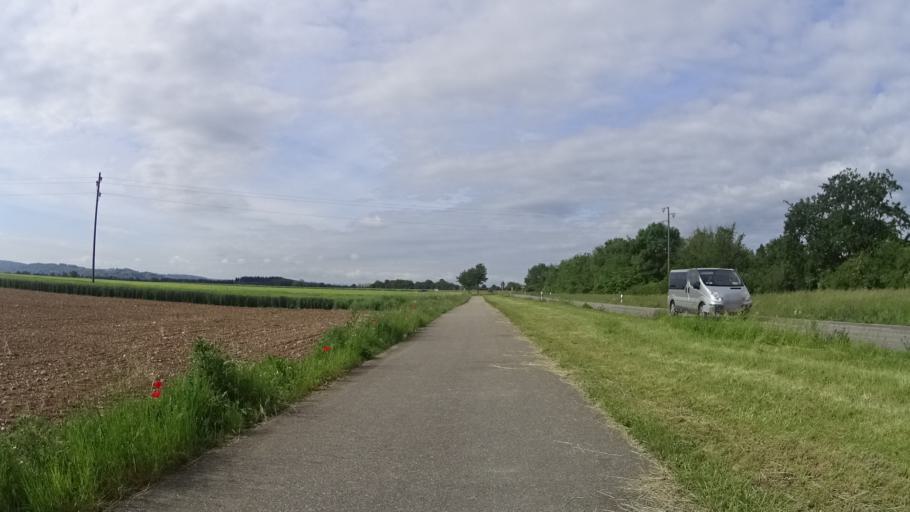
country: DE
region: Baden-Wuerttemberg
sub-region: Freiburg Region
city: Neuenburg am Rhein
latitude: 47.7989
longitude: 7.5589
